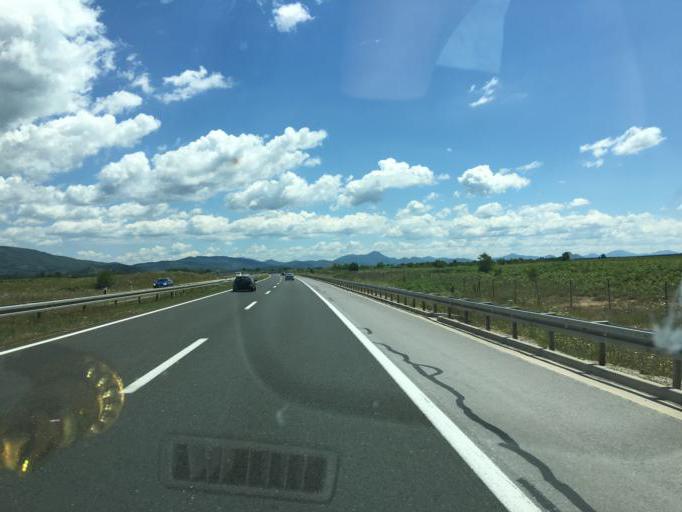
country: HR
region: Licko-Senjska
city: Gospic
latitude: 44.5177
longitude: 15.4765
